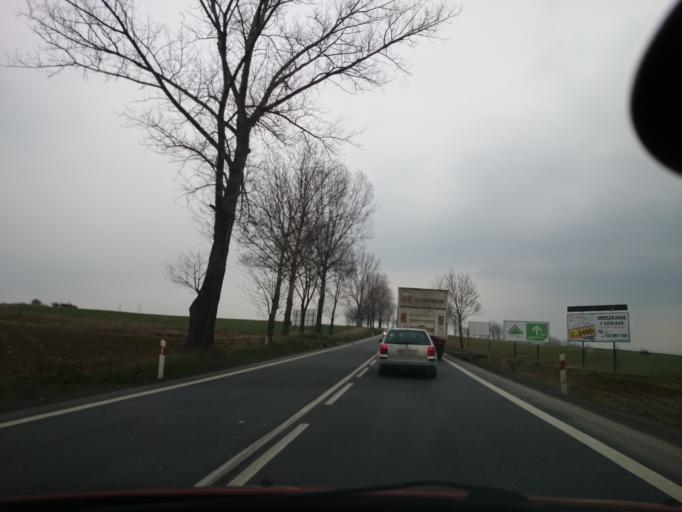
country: PL
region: Lower Silesian Voivodeship
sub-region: Powiat klodzki
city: Polanica-Zdroj
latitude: 50.4318
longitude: 16.5694
